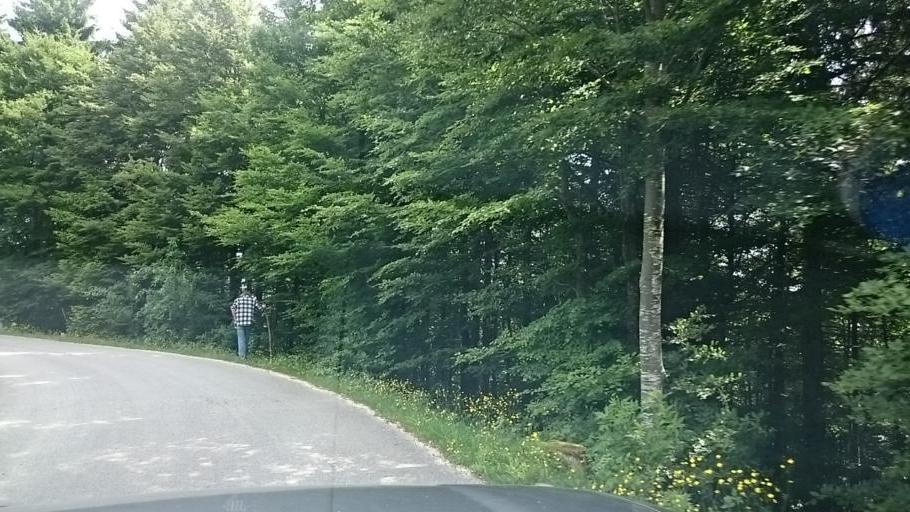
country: IT
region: Veneto
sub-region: Provincia di Vicenza
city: Foza
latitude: 45.9226
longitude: 11.6440
